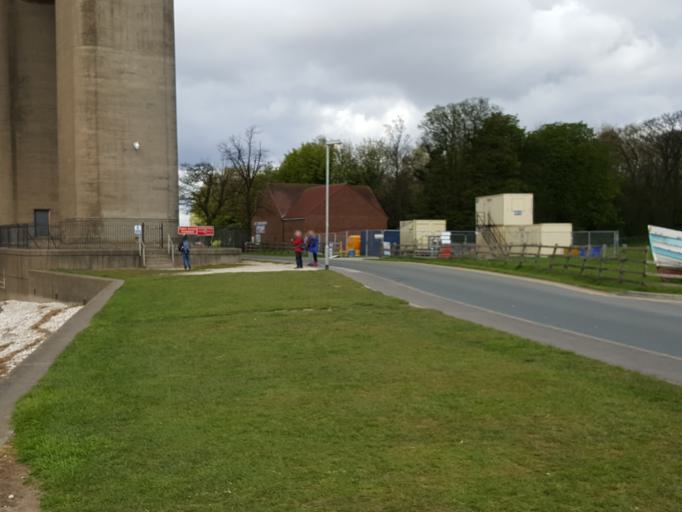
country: GB
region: England
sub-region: East Riding of Yorkshire
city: Hessle
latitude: 53.7141
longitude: -0.4496
